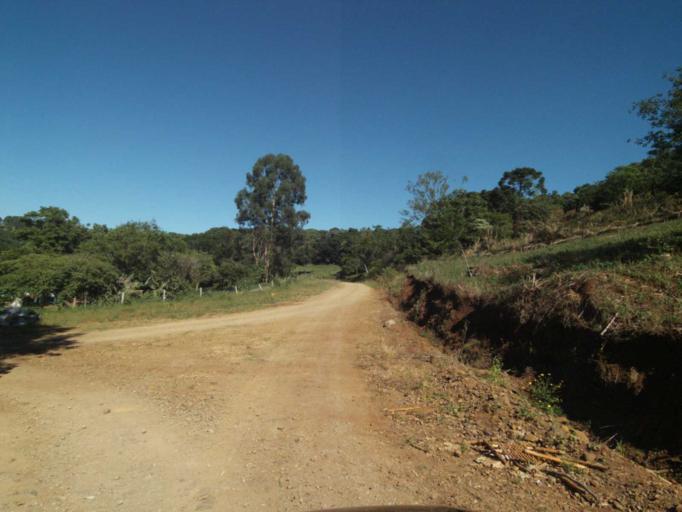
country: BR
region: Parana
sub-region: Francisco Beltrao
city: Francisco Beltrao
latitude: -26.1414
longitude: -53.3134
